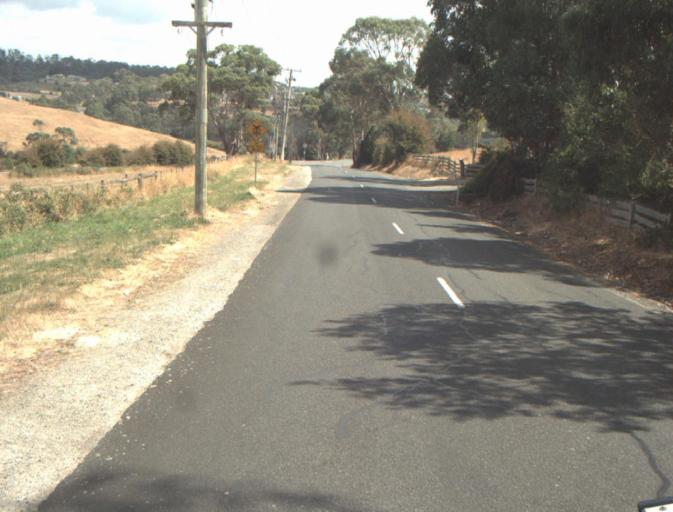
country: AU
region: Tasmania
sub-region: Launceston
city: Newstead
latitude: -41.4775
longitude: 147.1897
